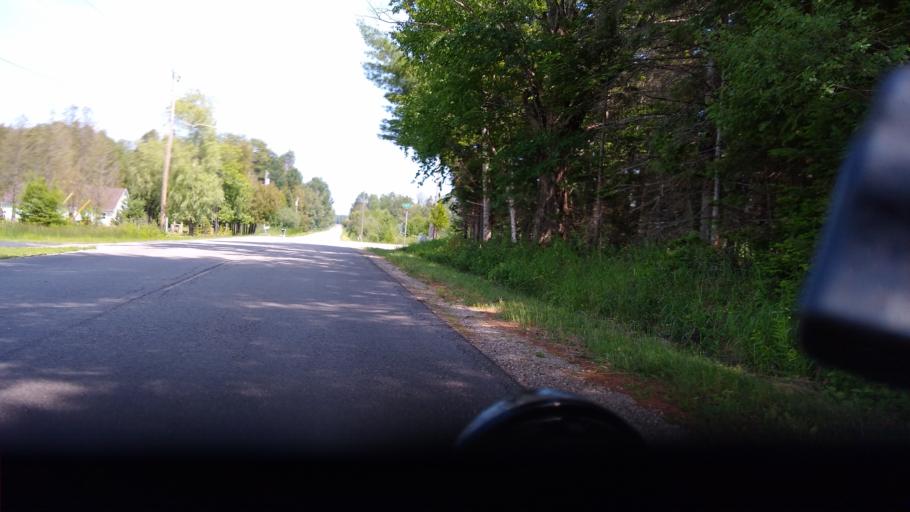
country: US
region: Michigan
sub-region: Delta County
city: Escanaba
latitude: 45.7101
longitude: -87.1224
